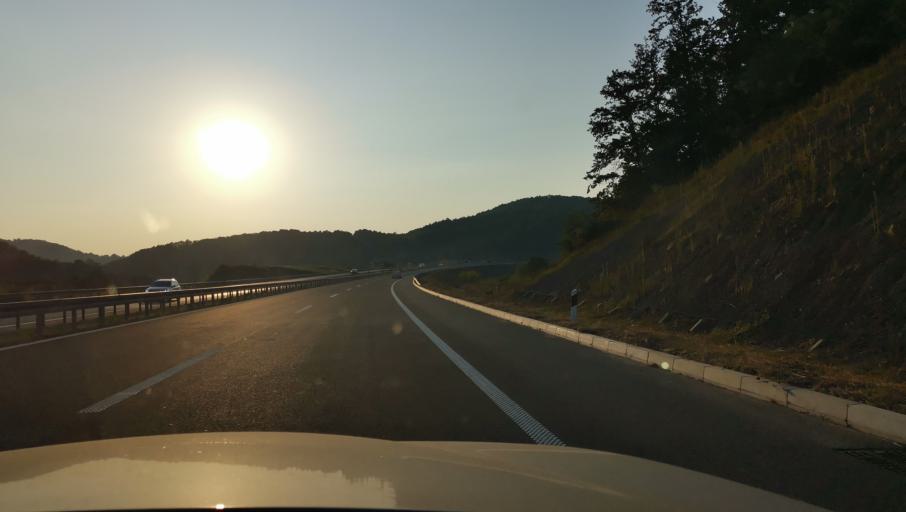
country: RS
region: Central Serbia
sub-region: Kolubarski Okrug
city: Ljig
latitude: 44.1991
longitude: 20.2737
